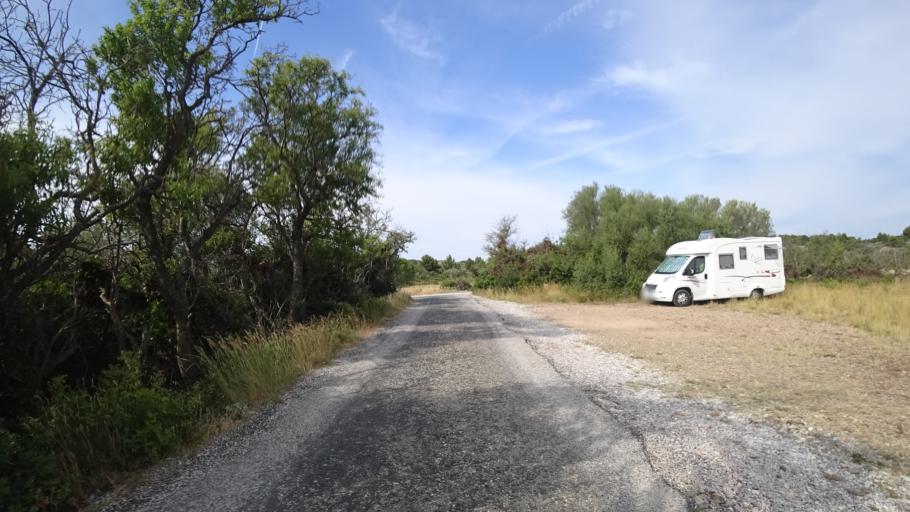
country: FR
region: Languedoc-Roussillon
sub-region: Departement de l'Aude
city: Leucate
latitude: 42.8988
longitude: 3.0279
